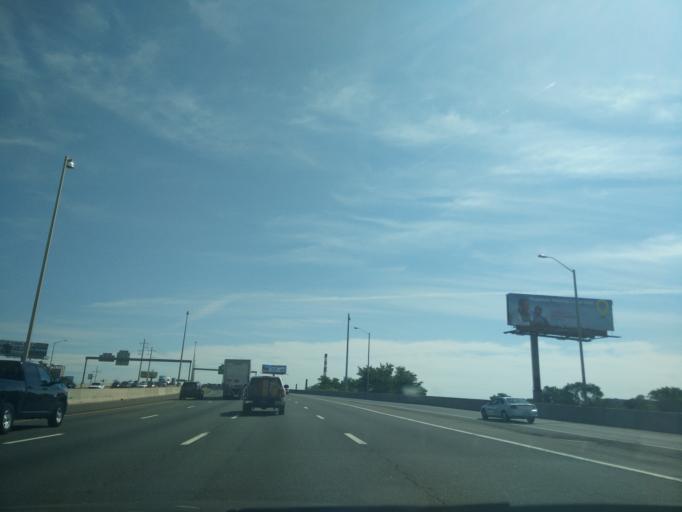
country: US
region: Connecticut
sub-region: Fairfield County
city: Bridgeport
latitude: 41.1670
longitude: -73.2031
